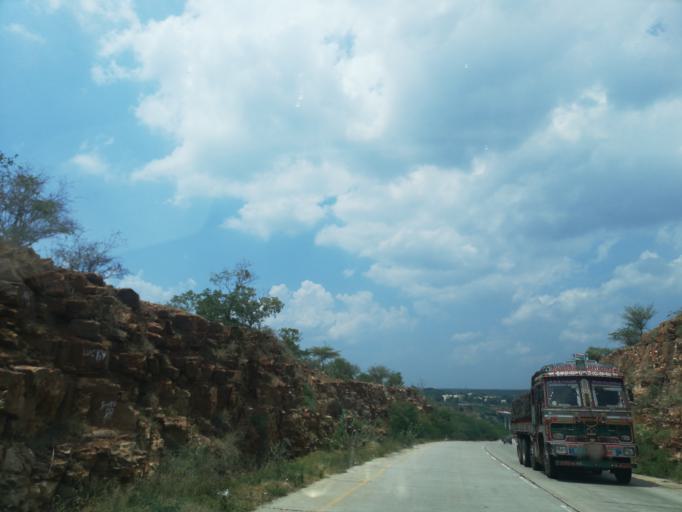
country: IN
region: Andhra Pradesh
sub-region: Guntur
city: Macherla
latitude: 16.5719
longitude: 79.3313
